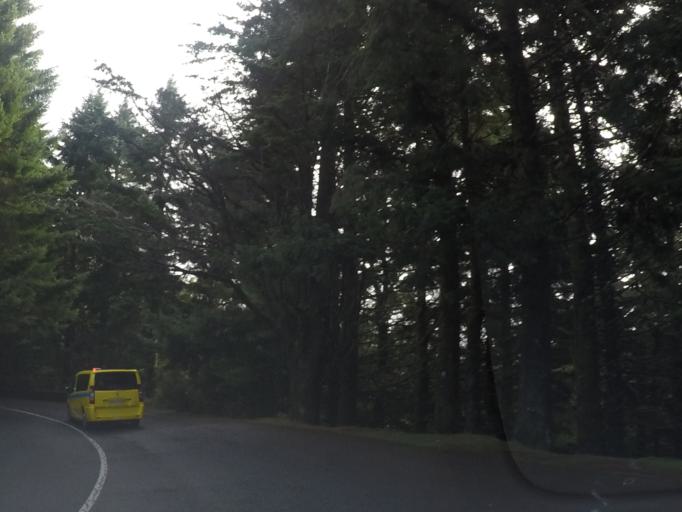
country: PT
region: Madeira
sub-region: Funchal
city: Nossa Senhora do Monte
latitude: 32.7060
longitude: -16.8937
